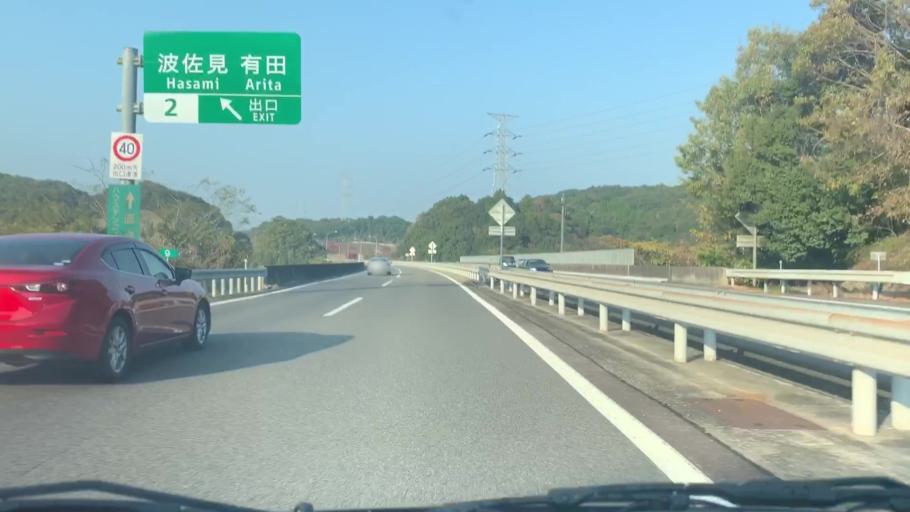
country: JP
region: Saga Prefecture
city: Ureshinomachi-shimojuku
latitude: 33.1565
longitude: 129.8986
